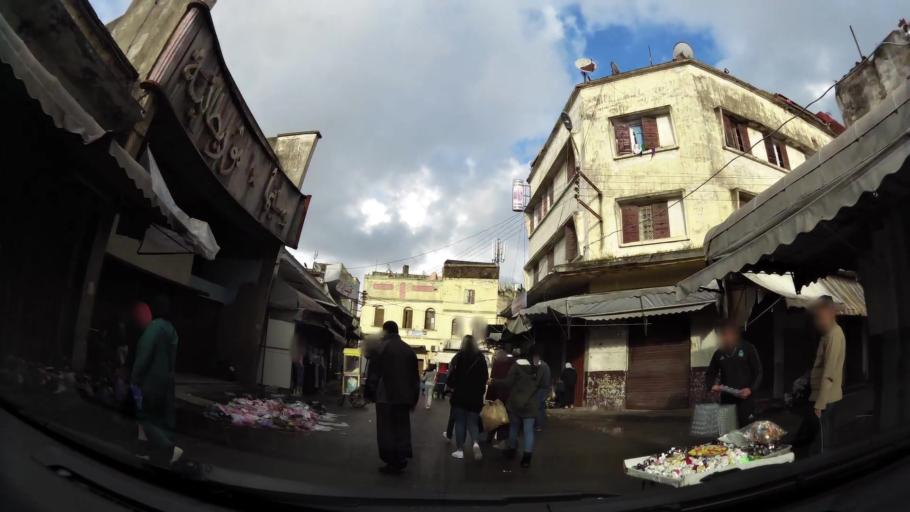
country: MA
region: Grand Casablanca
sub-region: Casablanca
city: Casablanca
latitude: 33.5738
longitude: -7.6023
